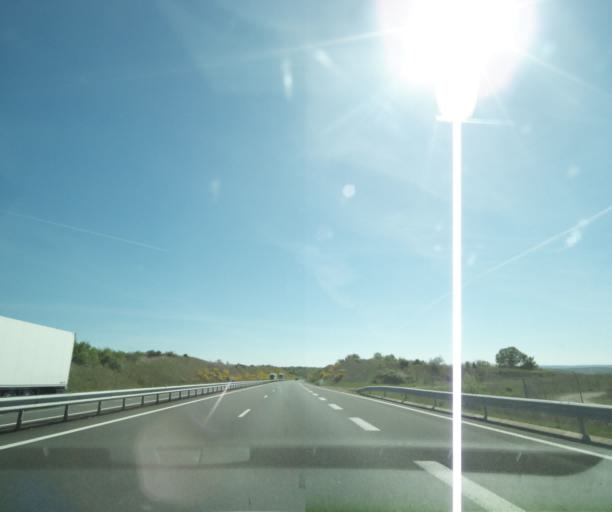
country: FR
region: Midi-Pyrenees
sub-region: Departement du Lot
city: Cahors
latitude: 44.5266
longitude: 1.5115
